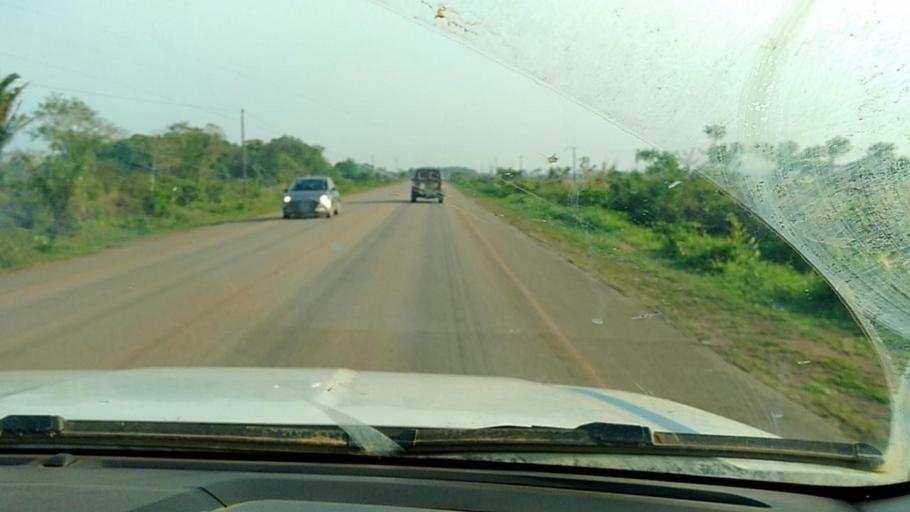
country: BR
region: Rondonia
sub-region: Porto Velho
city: Porto Velho
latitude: -8.6597
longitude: -63.9957
